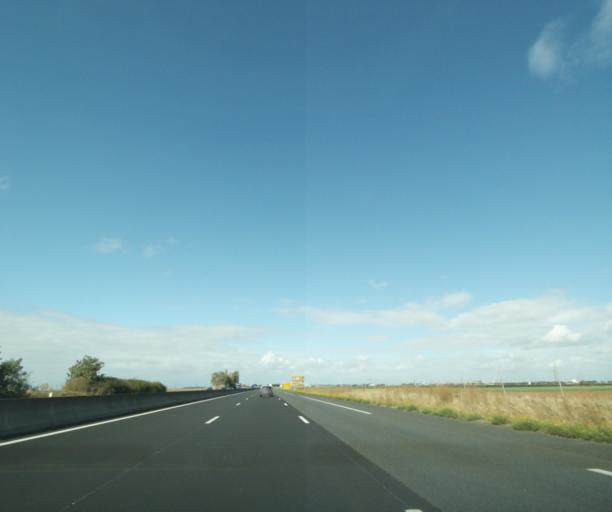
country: FR
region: Centre
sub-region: Departement du Loiret
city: Artenay
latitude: 48.0618
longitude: 1.8455
